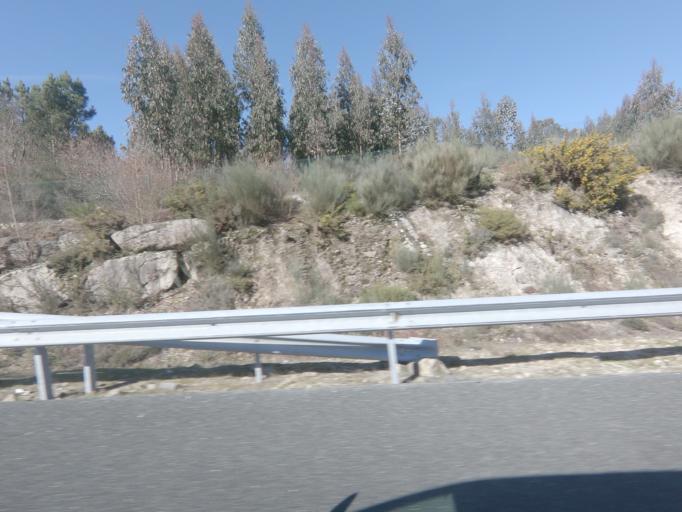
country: ES
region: Galicia
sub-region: Provincia de Ourense
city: Pinor
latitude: 42.5048
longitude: -8.0245
